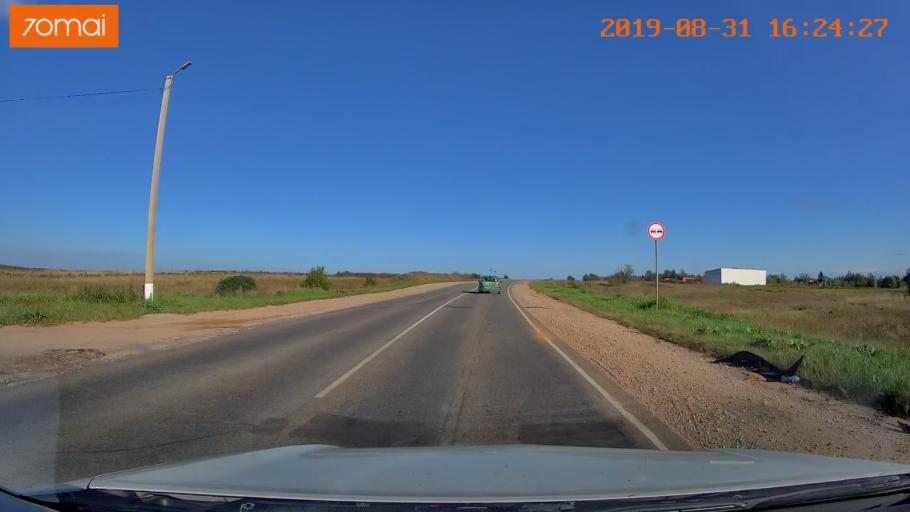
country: RU
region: Kaluga
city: Babynino
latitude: 54.5221
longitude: 35.6955
